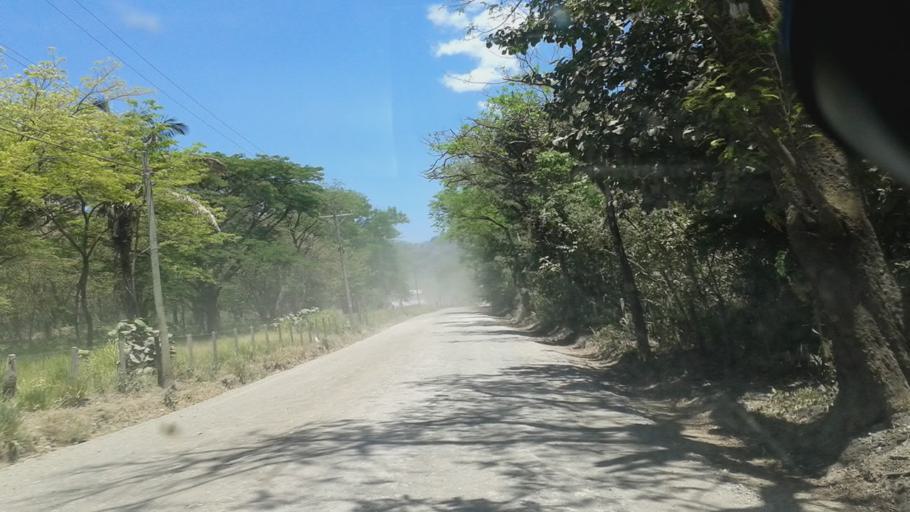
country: CR
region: Guanacaste
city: Samara
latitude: 9.9933
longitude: -85.6804
